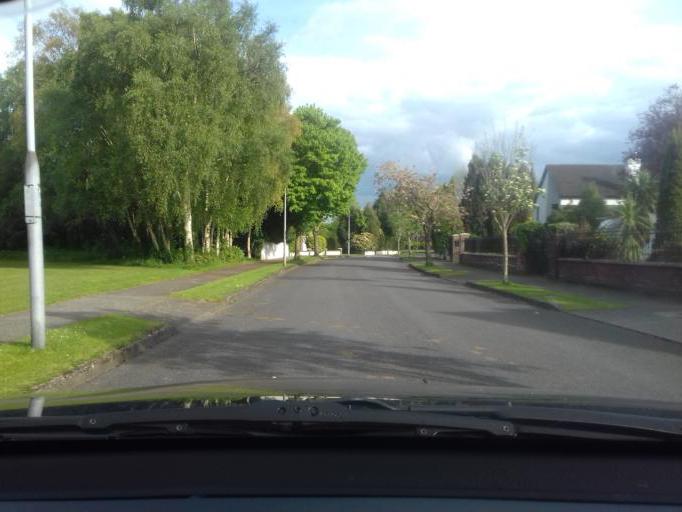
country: IE
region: Leinster
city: Castleknock
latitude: 53.3733
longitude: -6.3490
